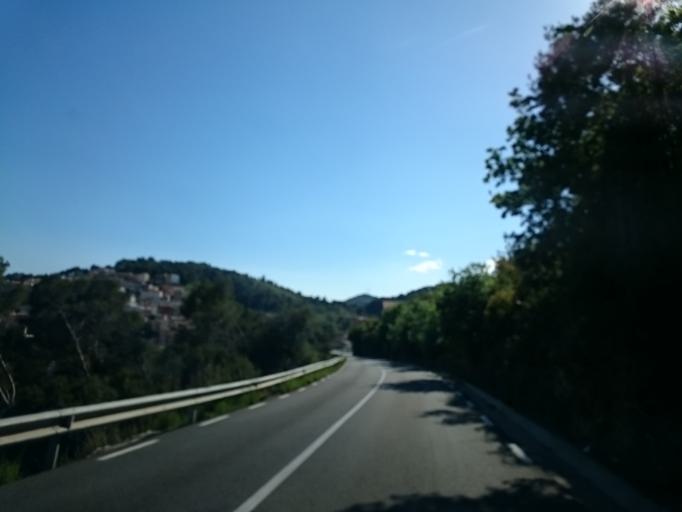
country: ES
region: Catalonia
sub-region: Provincia de Barcelona
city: Torrelles de Llobregat
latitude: 41.3395
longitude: 2.0010
